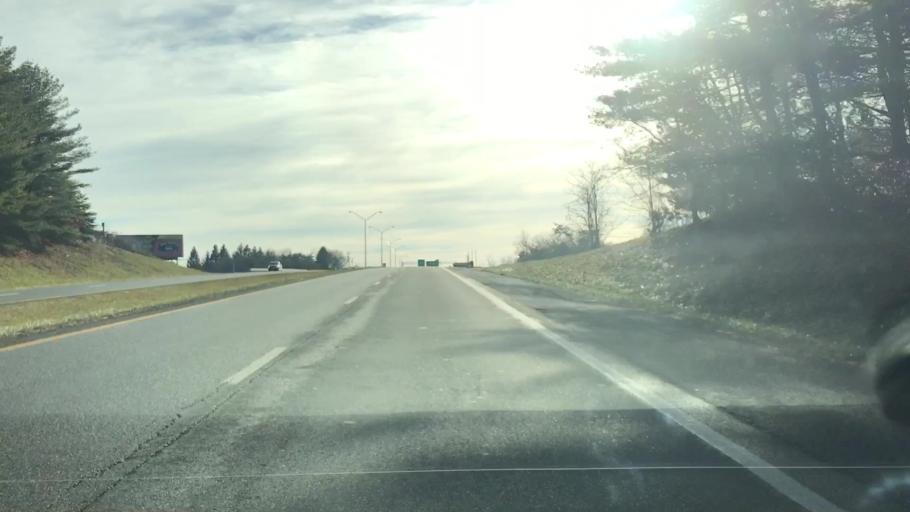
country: US
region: Virginia
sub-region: Montgomery County
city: Christiansburg
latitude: 37.1389
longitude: -80.3816
